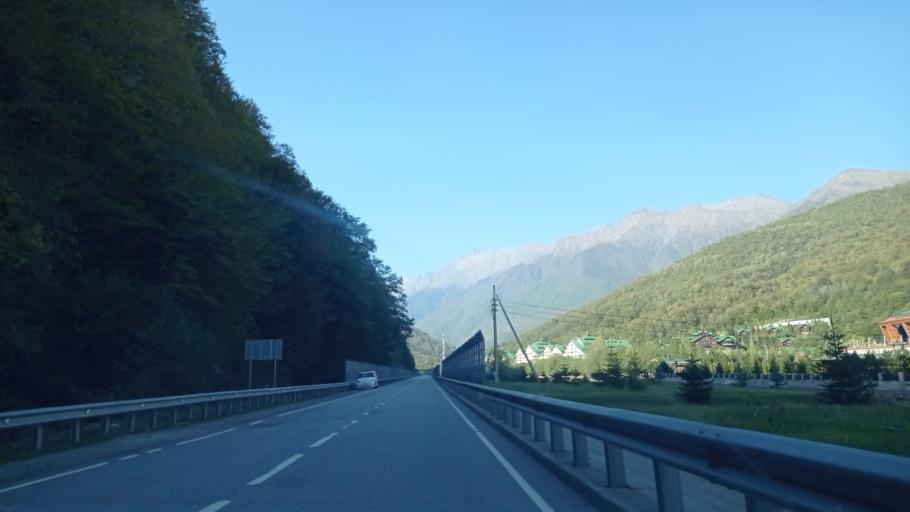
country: RU
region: Krasnodarskiy
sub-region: Sochi City
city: Krasnaya Polyana
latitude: 43.6838
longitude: 40.2780
